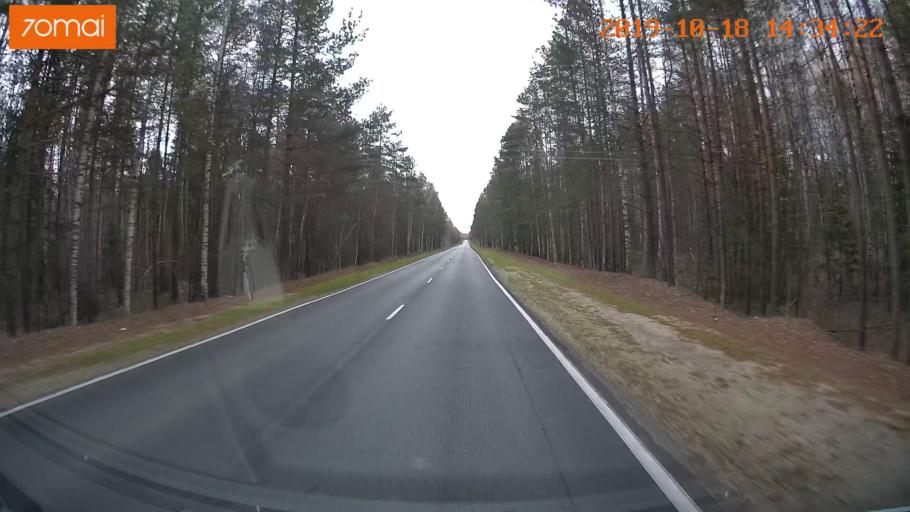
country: RU
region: Vladimir
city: Velikodvorskiy
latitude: 55.2114
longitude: 40.6147
